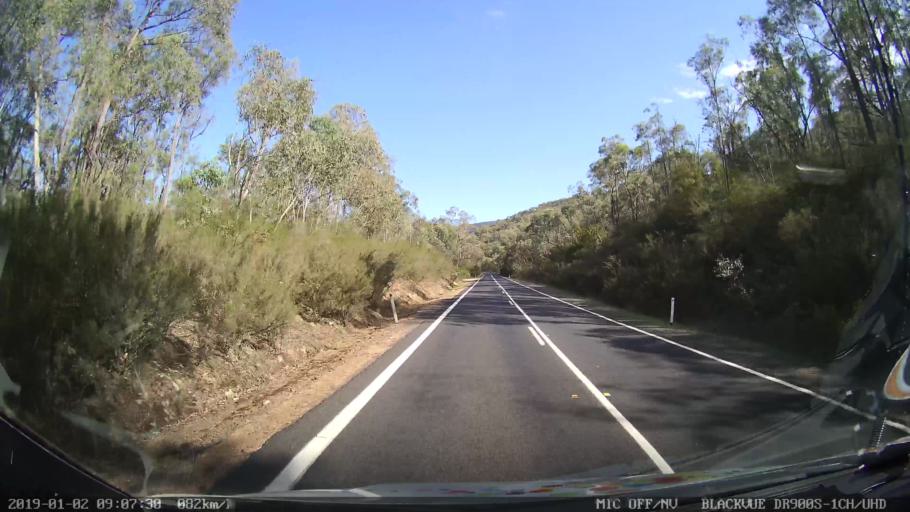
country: AU
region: New South Wales
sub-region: Tumut Shire
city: Tumut
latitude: -35.5403
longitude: 148.2978
